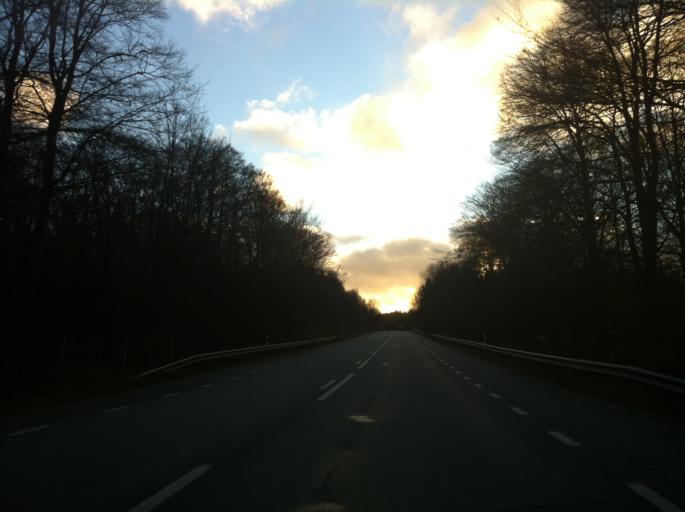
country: SE
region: Skane
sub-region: Hassleholms Kommun
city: Sosdala
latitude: 56.0054
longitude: 13.6498
